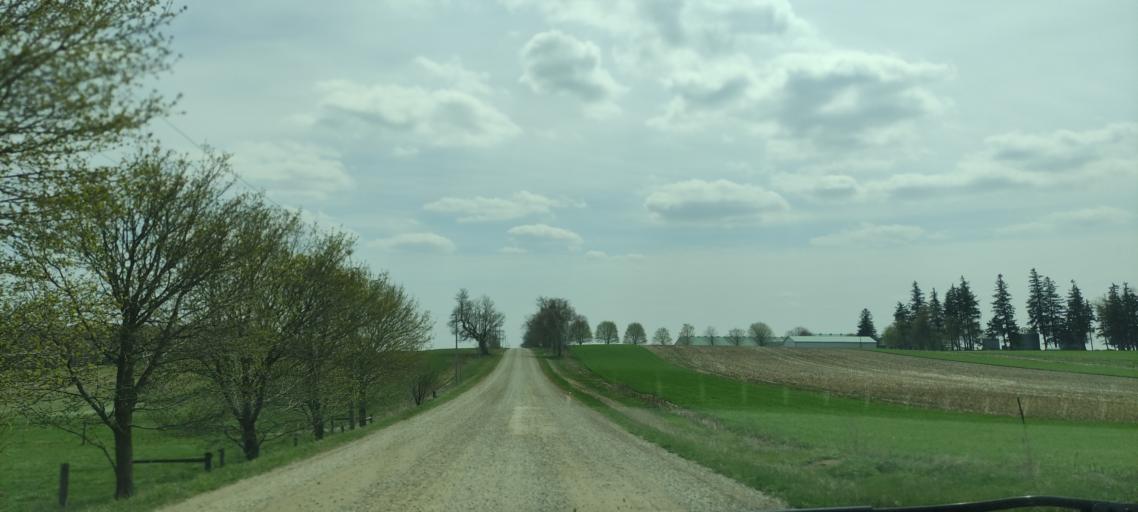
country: CA
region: Ontario
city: Stratford
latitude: 43.3495
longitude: -80.7453
